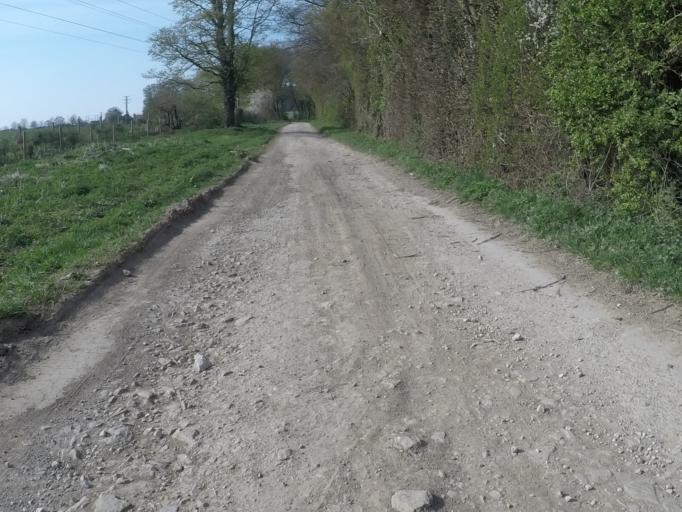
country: GB
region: England
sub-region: Oxfordshire
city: Charlbury
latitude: 51.8867
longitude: -1.4531
